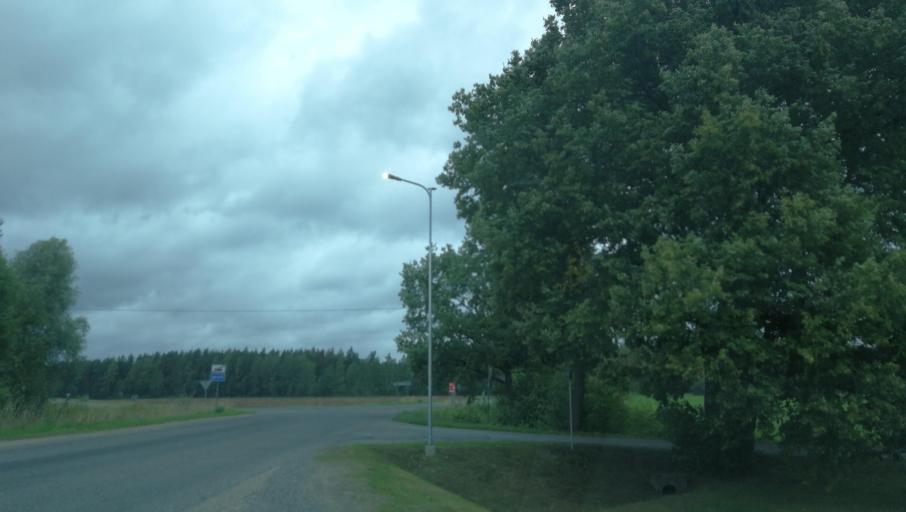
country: LV
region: Beverina
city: Murmuiza
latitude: 57.4943
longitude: 25.4470
